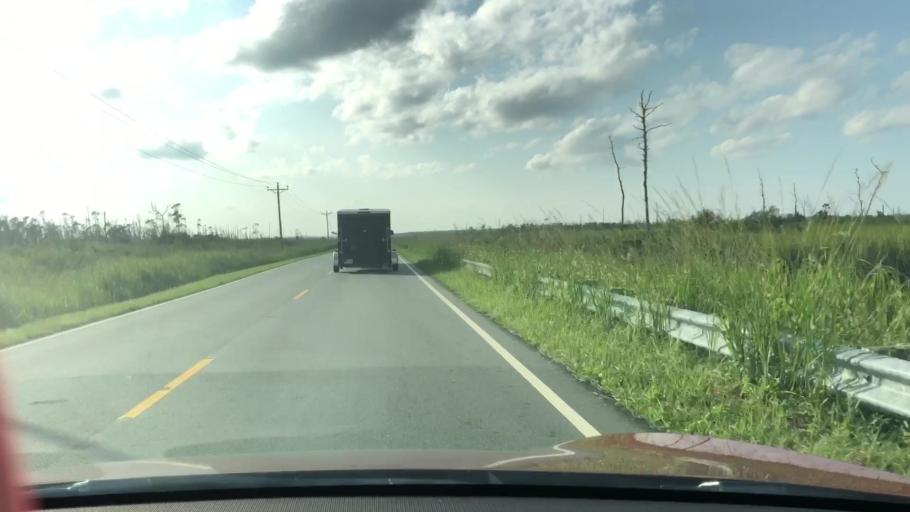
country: US
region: North Carolina
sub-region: Dare County
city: Wanchese
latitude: 35.6237
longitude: -75.8433
